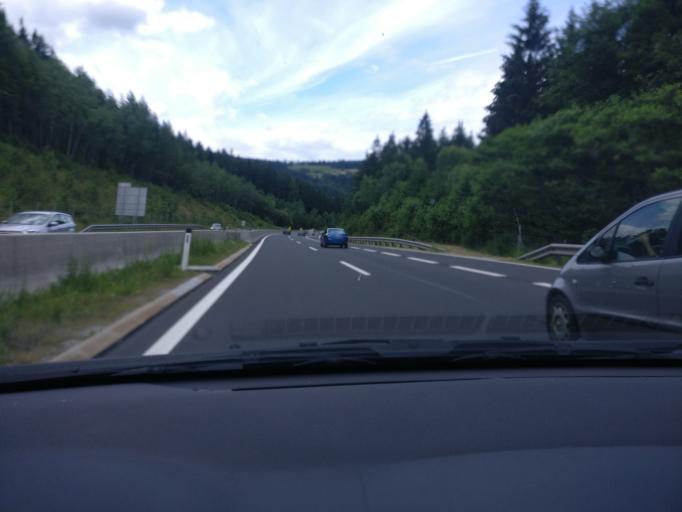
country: AT
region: Lower Austria
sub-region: Politischer Bezirk Neunkirchen
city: Zobern
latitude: 47.4894
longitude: 16.0984
